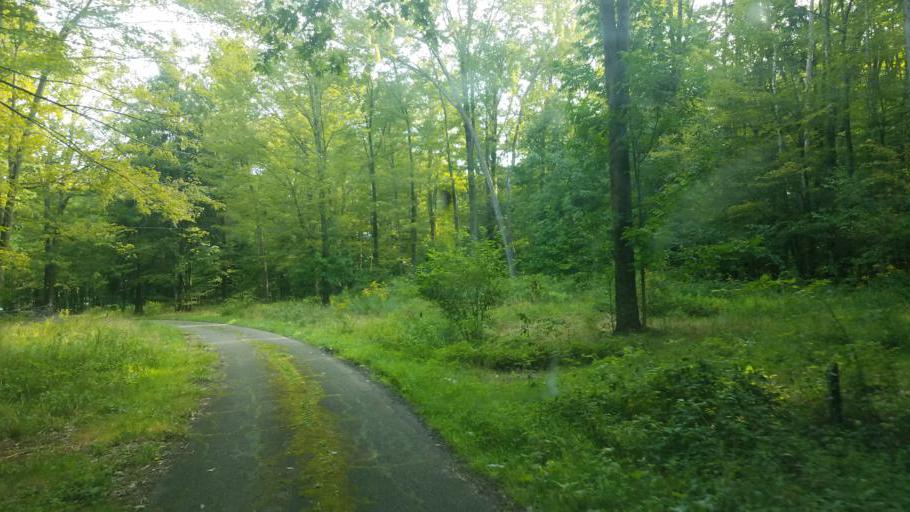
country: US
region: Pennsylvania
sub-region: Crawford County
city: Pymatuning Central
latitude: 41.6424
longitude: -80.4906
